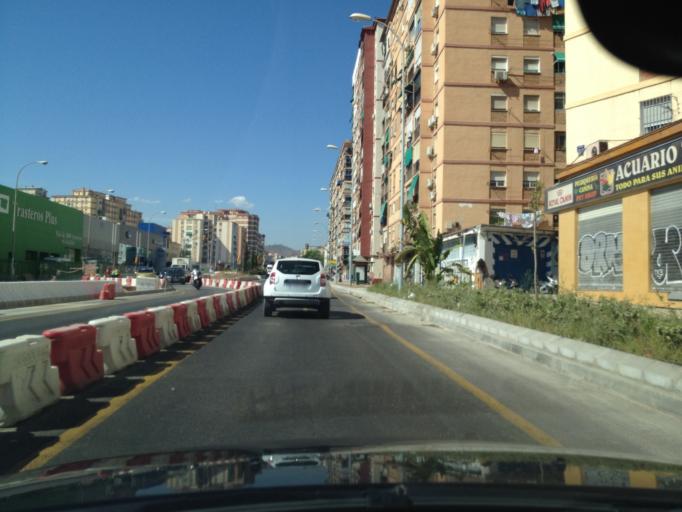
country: ES
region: Andalusia
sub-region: Provincia de Malaga
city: Malaga
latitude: 36.7077
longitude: -4.4434
